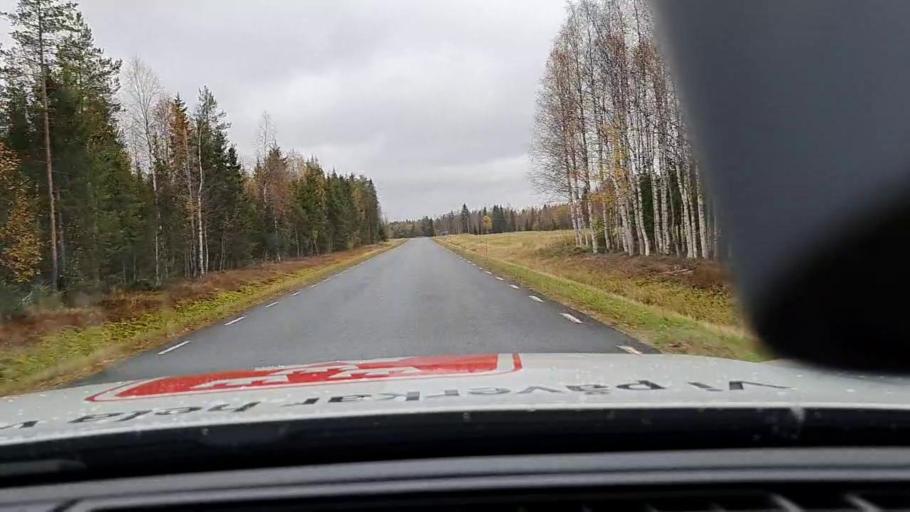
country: SE
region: Norrbotten
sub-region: Haparanda Kommun
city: Haparanda
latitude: 65.9302
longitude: 23.8168
